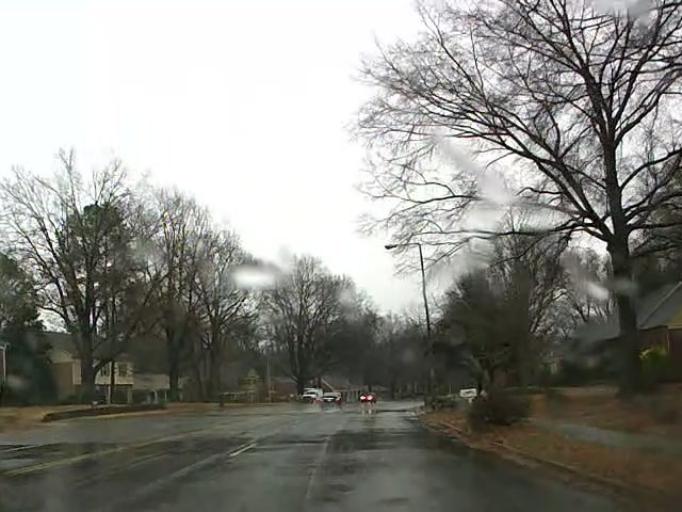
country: US
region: Tennessee
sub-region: Shelby County
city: Germantown
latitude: 35.0858
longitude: -89.8553
